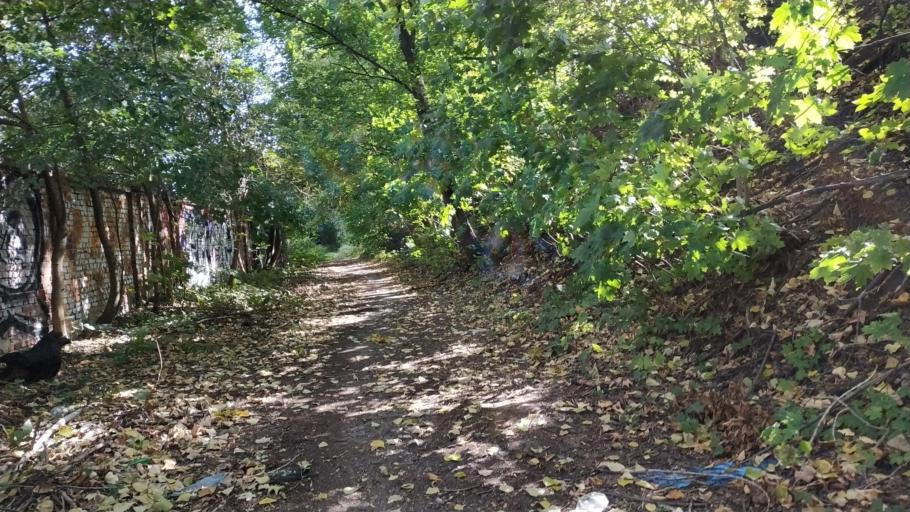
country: PL
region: Lower Silesian Voivodeship
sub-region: Powiat wroclawski
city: Wroclaw
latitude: 51.0712
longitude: 17.0209
